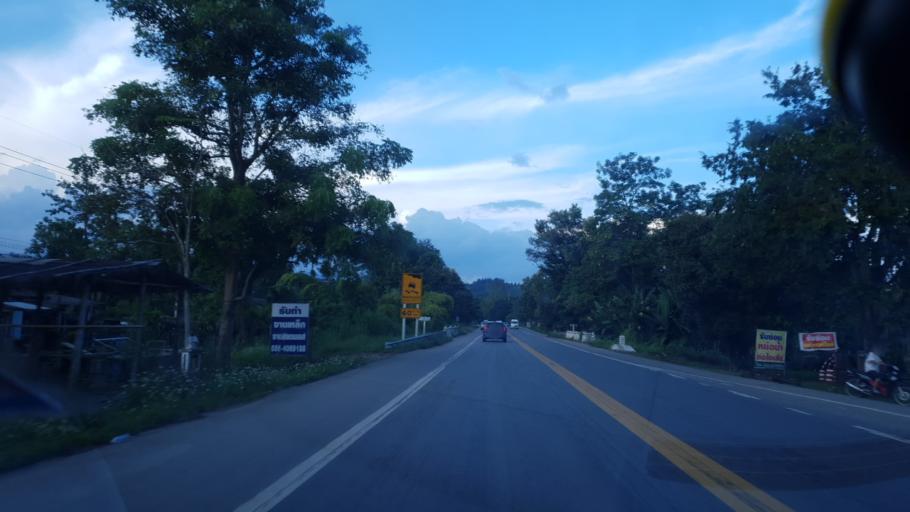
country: TH
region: Chiang Rai
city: Mae Suai
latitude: 19.6631
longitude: 99.5495
